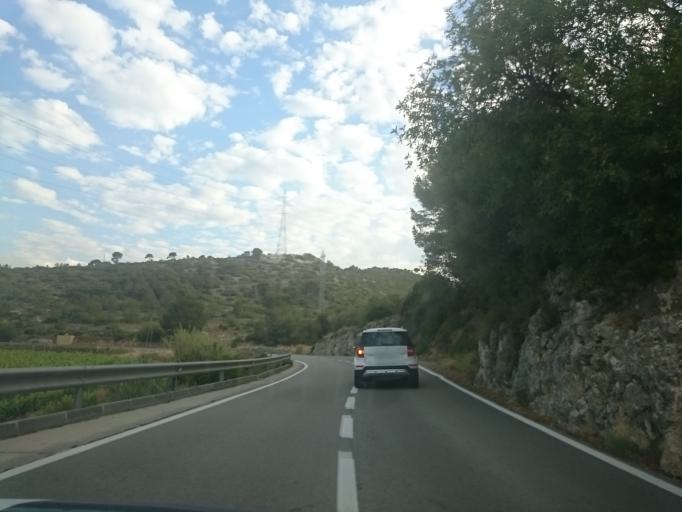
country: ES
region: Catalonia
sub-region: Provincia de Barcelona
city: Cubelles
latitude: 41.2316
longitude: 1.6687
